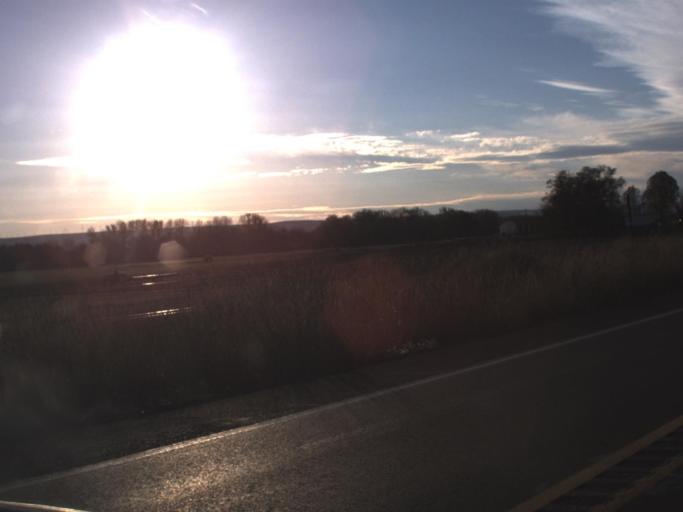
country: US
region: Washington
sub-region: Walla Walla County
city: Garrett
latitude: 46.0499
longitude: -118.5268
